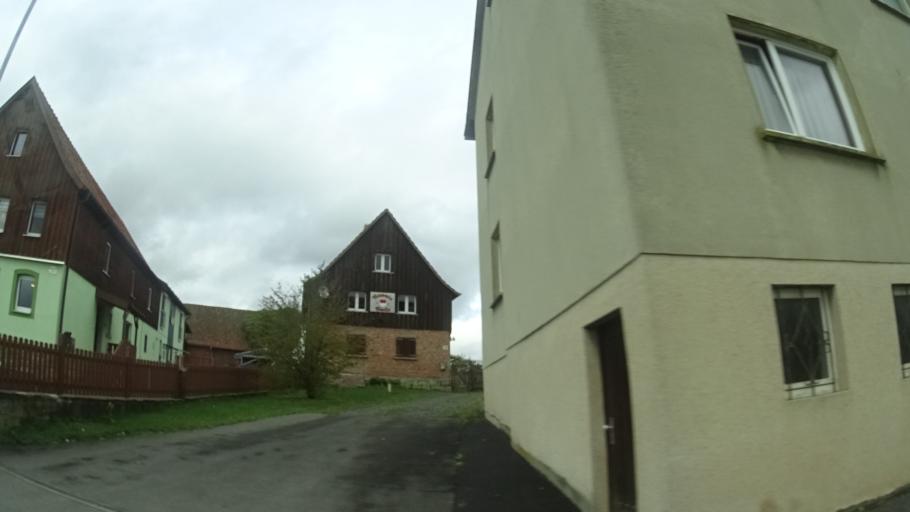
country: DE
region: Bavaria
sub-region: Regierungsbezirk Unterfranken
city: Bad Neustadt an der Saale
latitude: 50.3308
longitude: 10.1982
